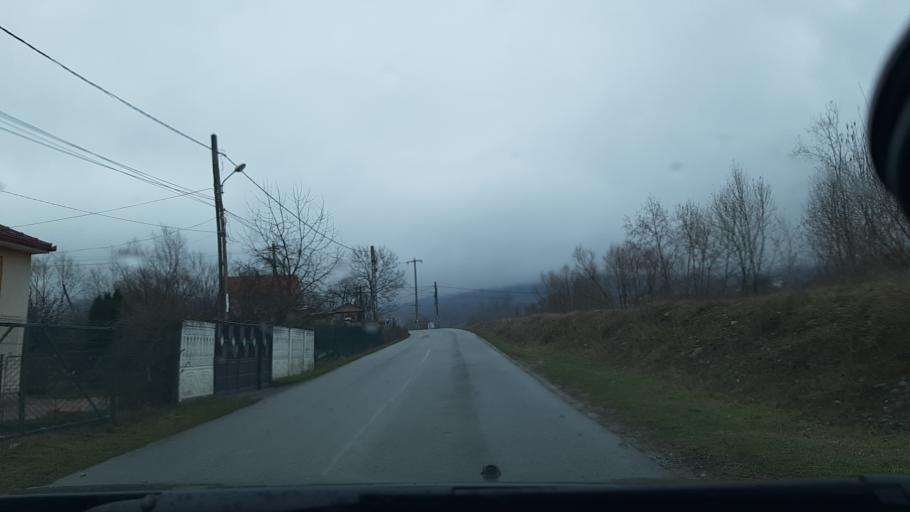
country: RO
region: Hunedoara
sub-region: Oras Petrila
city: Petrila
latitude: 45.4265
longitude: 23.4234
